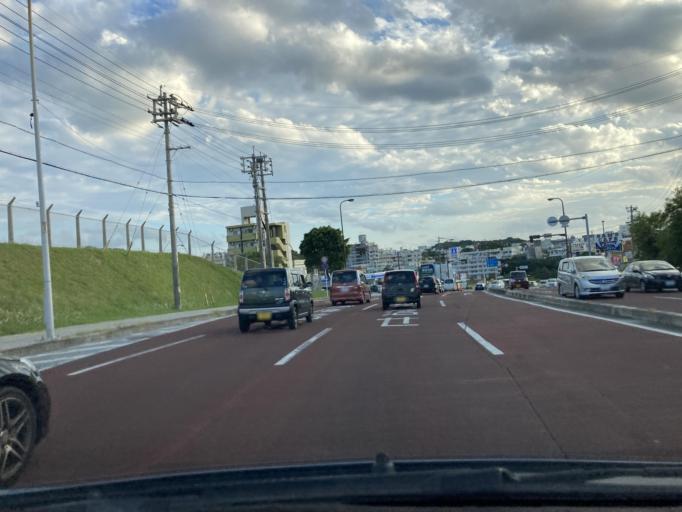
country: JP
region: Okinawa
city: Chatan
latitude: 26.2974
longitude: 127.7807
